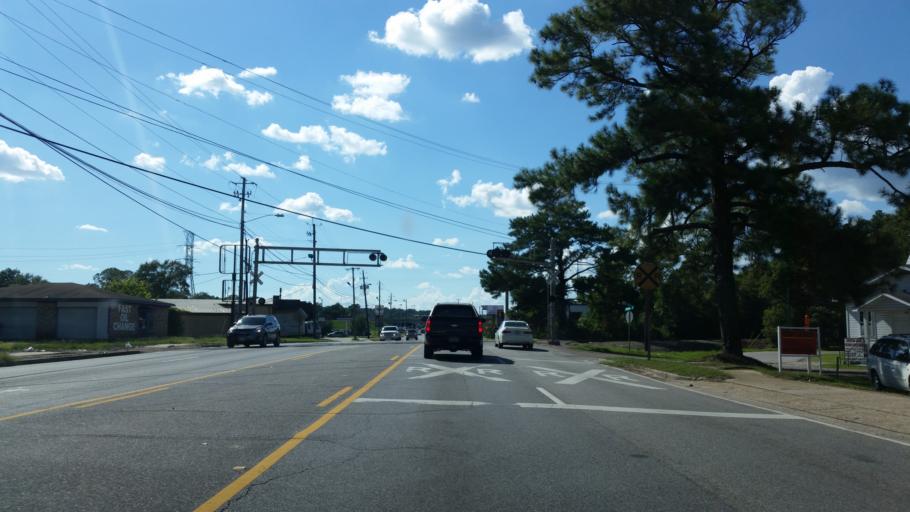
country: US
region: Alabama
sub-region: Mobile County
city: Prichard
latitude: 30.7024
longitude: -88.1189
